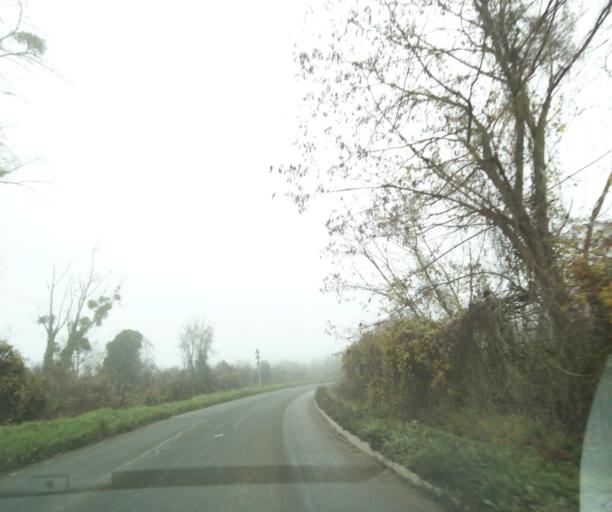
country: FR
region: Ile-de-France
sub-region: Departement de Seine-et-Marne
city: Courtry
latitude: 48.9221
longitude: 2.5956
